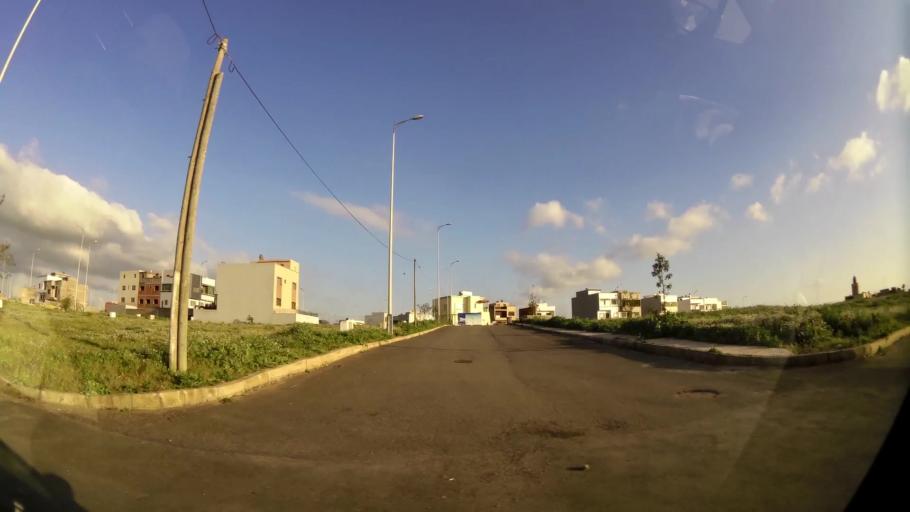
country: MA
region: Chaouia-Ouardigha
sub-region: Settat Province
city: Settat
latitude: 33.0132
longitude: -7.6016
